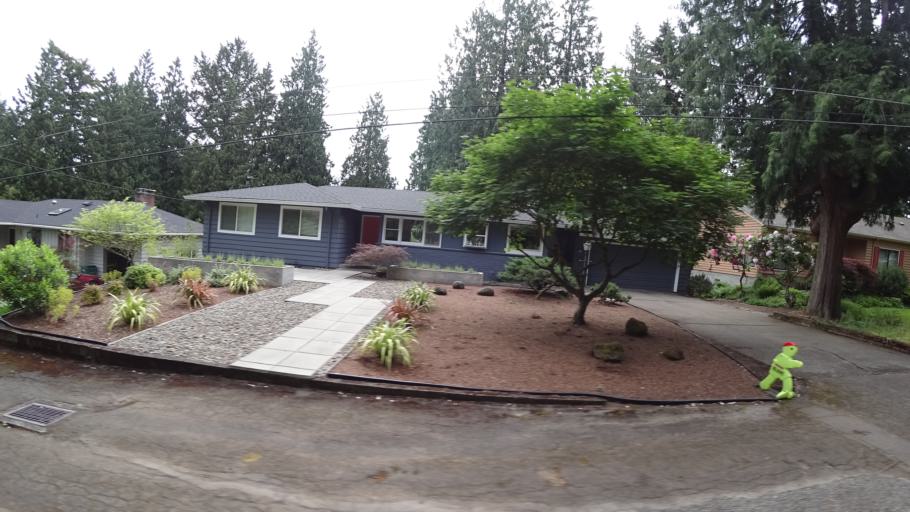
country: US
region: Oregon
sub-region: Washington County
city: Garden Home-Whitford
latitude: 45.4704
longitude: -122.7475
